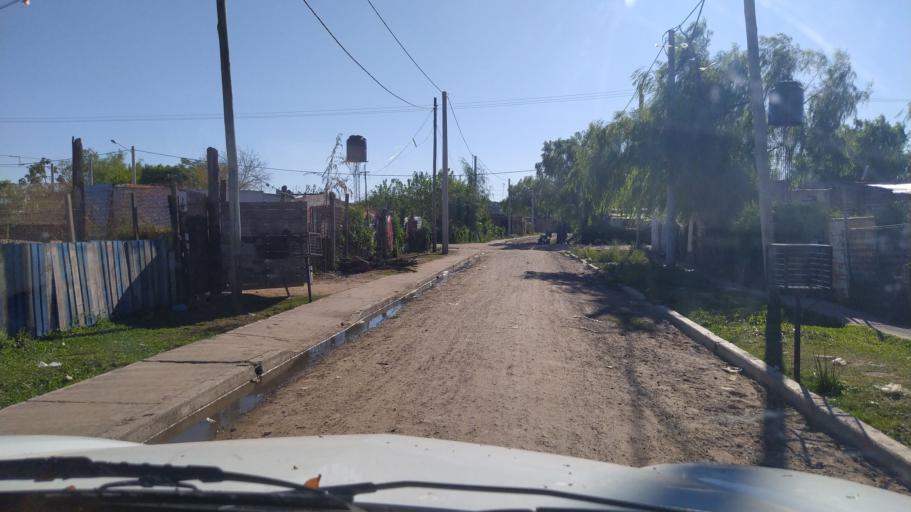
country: AR
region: Corrientes
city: Corrientes
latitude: -27.4963
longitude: -58.8041
